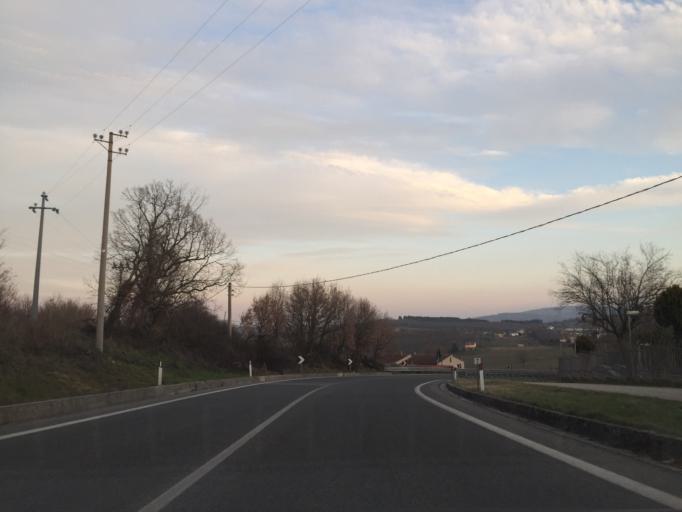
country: IT
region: Molise
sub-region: Provincia di Campobasso
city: Campobasso
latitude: 41.5605
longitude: 14.7003
